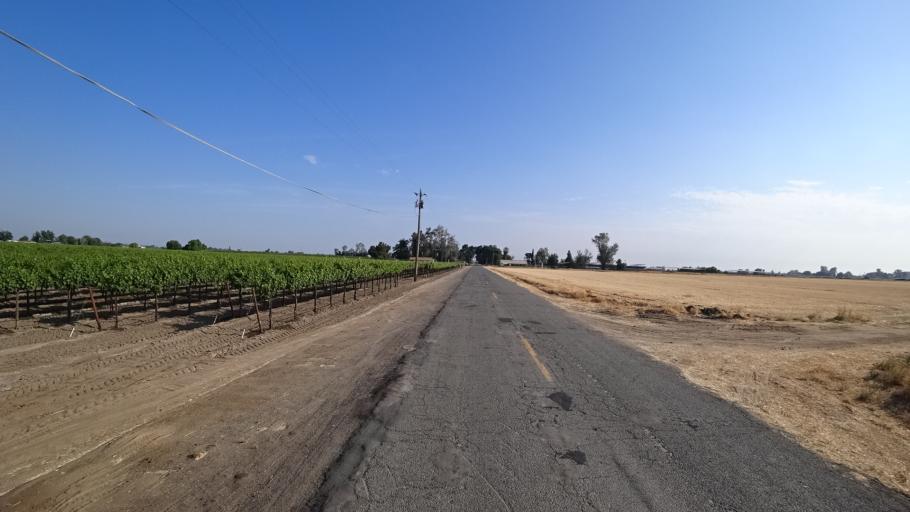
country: US
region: California
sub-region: Fresno County
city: Riverdale
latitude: 36.3693
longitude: -119.8431
